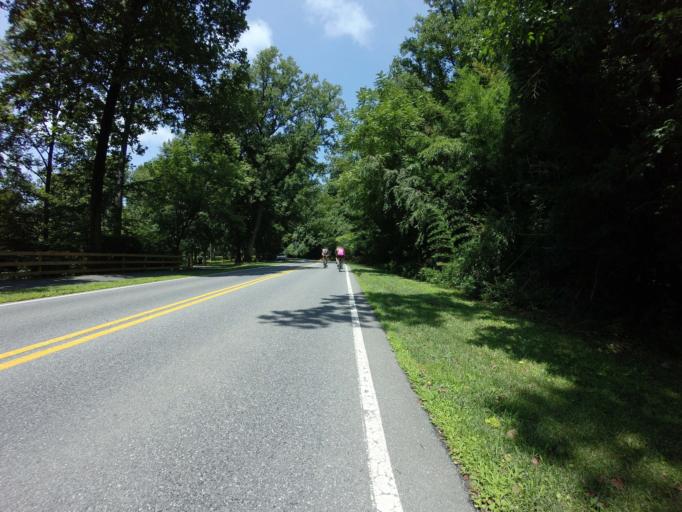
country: US
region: Maryland
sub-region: Montgomery County
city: South Kensington
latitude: 39.0162
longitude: -77.0943
